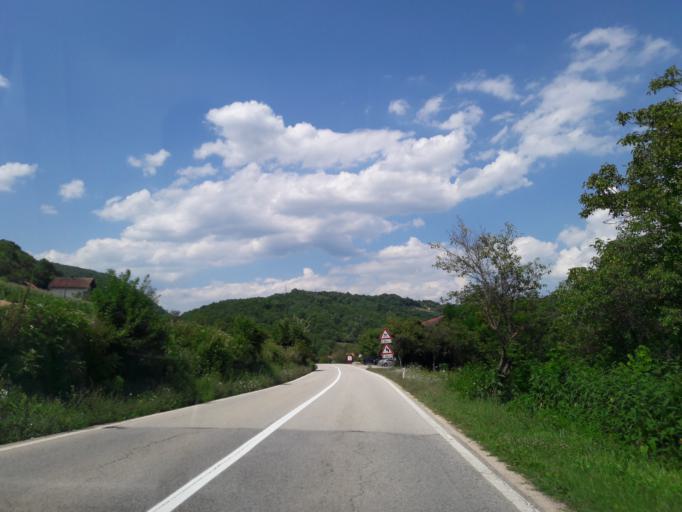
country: BA
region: Republika Srpska
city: Mrkonjic Grad
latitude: 44.5370
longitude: 17.1492
